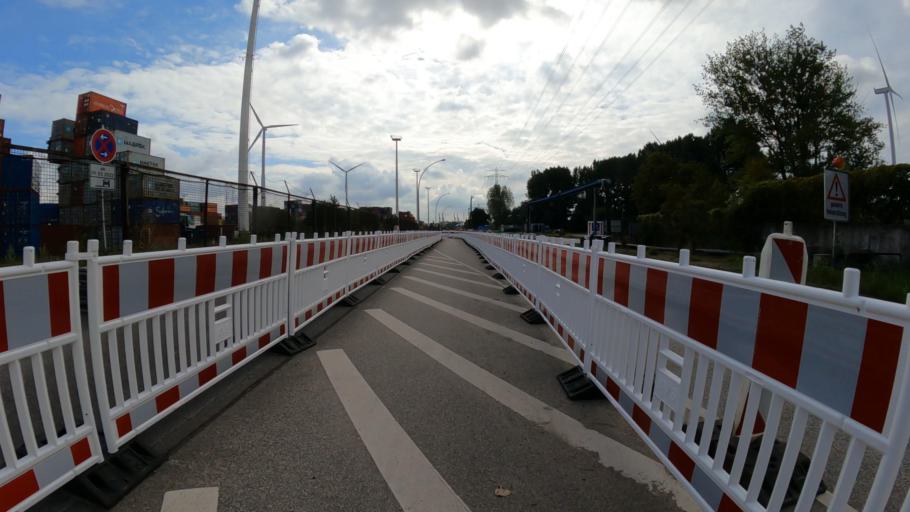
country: DE
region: Hamburg
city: Altona
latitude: 53.5234
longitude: 9.9041
